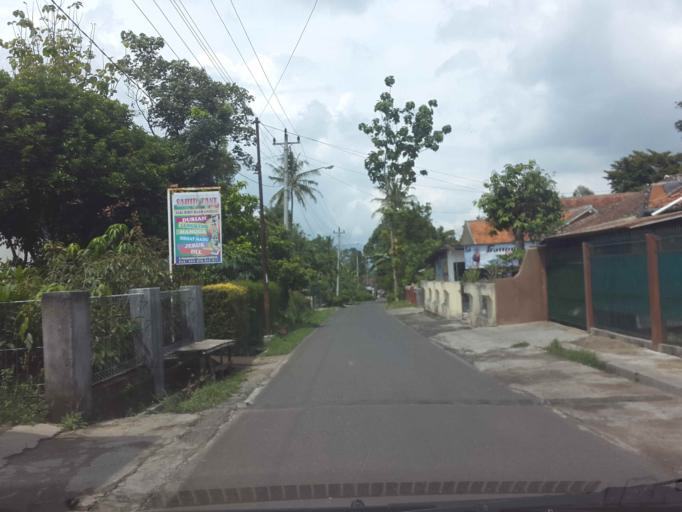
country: ID
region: Central Java
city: Salatiga
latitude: -7.3424
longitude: 110.5047
